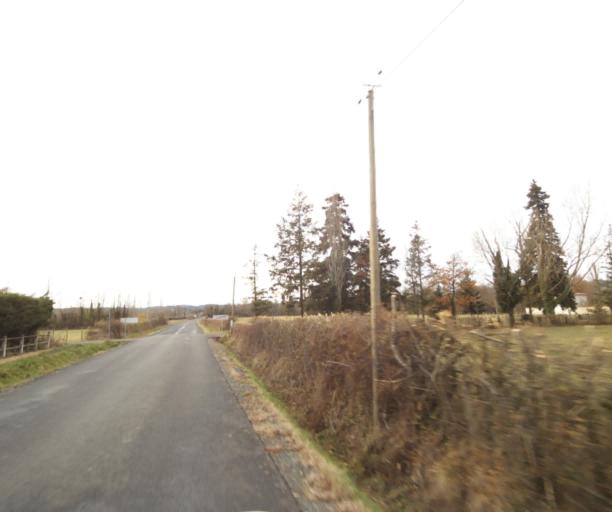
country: FR
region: Rhone-Alpes
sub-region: Departement de la Loire
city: Sury-le-Comtal
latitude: 45.5197
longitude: 4.1813
